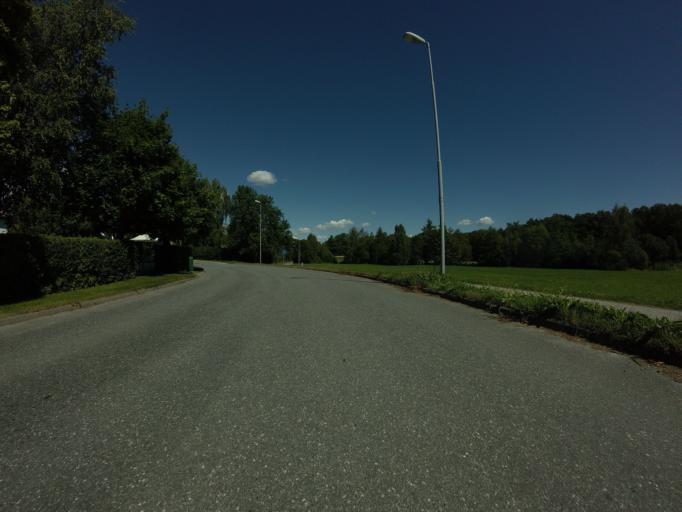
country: SE
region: Stockholm
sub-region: Sollentuna Kommun
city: Sollentuna
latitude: 59.4566
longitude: 17.9024
